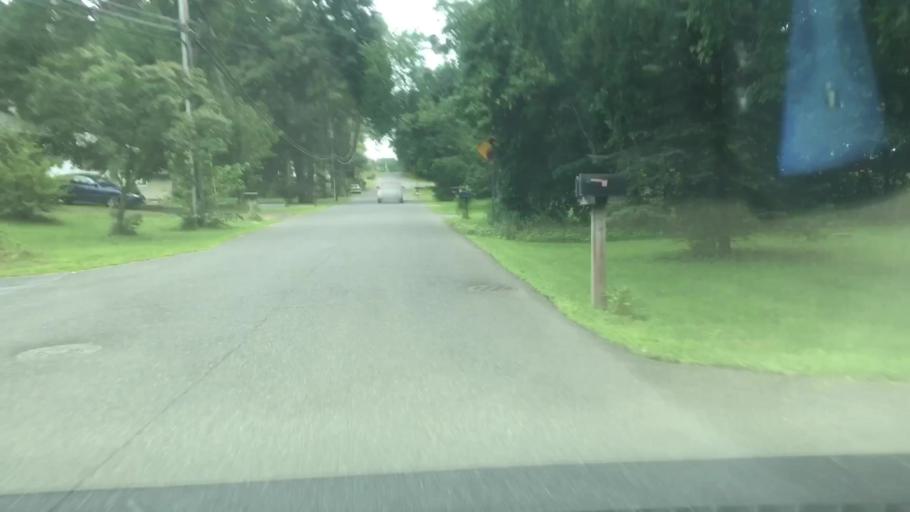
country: US
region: New York
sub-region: Schenectady County
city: Rotterdam
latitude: 42.7320
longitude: -73.9368
